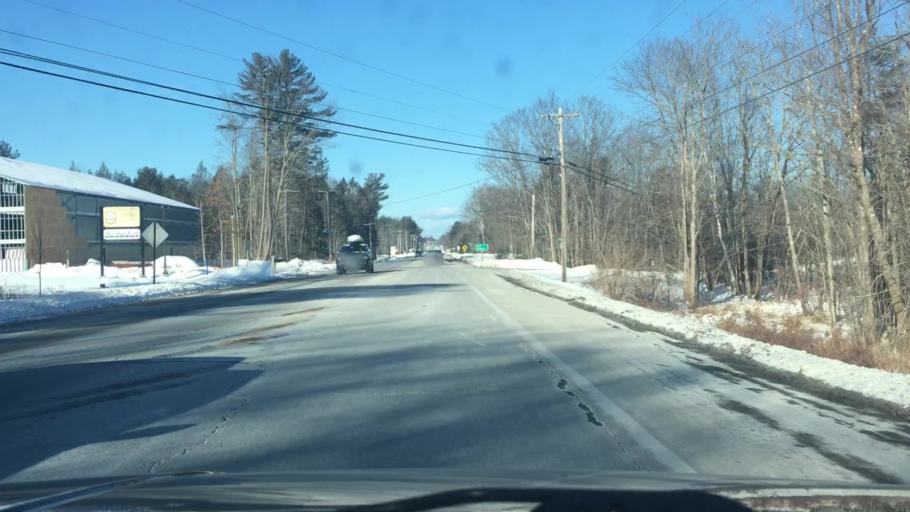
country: US
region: Maine
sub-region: York County
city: South Eliot
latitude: 43.1187
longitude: -70.7573
